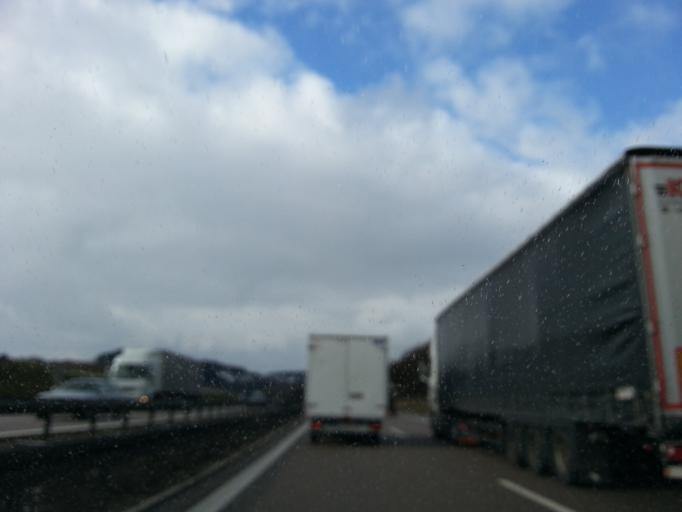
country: DE
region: Bavaria
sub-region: Upper Palatinate
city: Velburg
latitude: 49.2429
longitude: 11.6310
